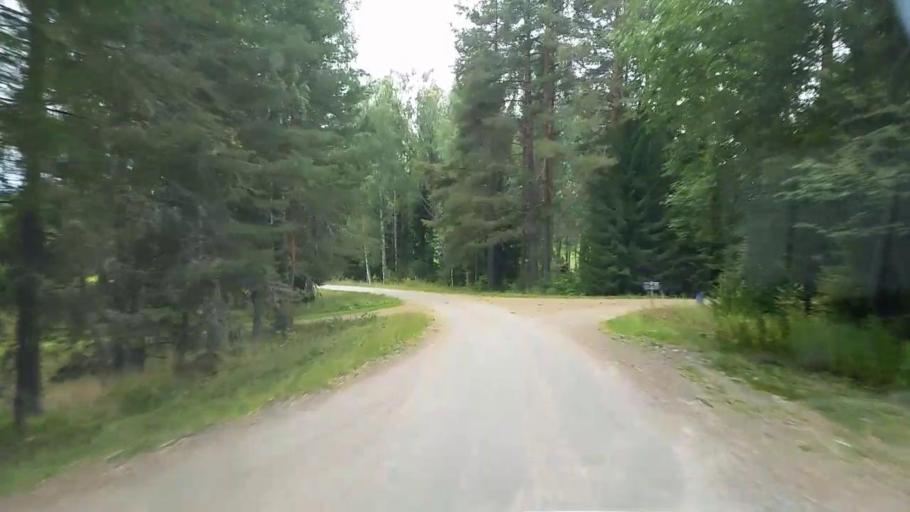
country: SE
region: Gaevleborg
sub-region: Ljusdals Kommun
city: Farila
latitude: 61.8115
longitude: 15.8647
